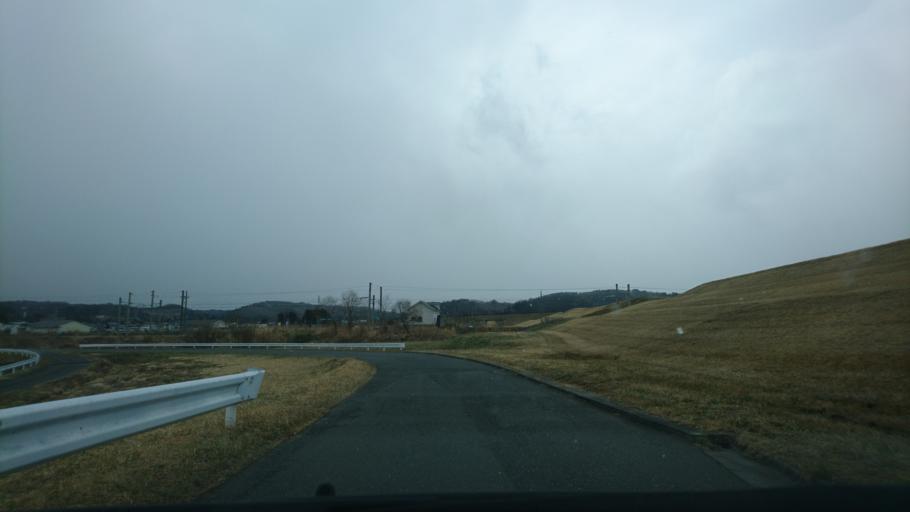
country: JP
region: Iwate
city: Ichinoseki
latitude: 38.9849
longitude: 141.1204
